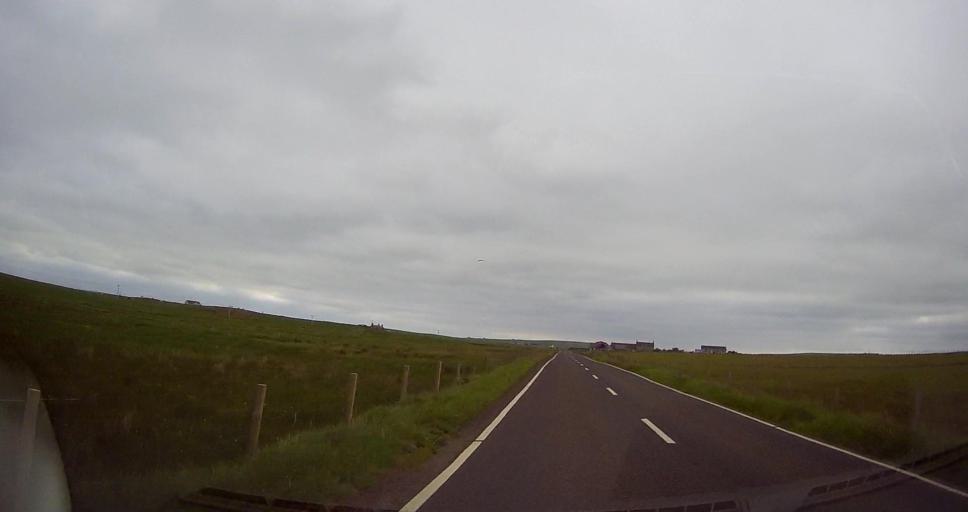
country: GB
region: Scotland
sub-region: Orkney Islands
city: Kirkwall
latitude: 58.9336
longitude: -2.8536
